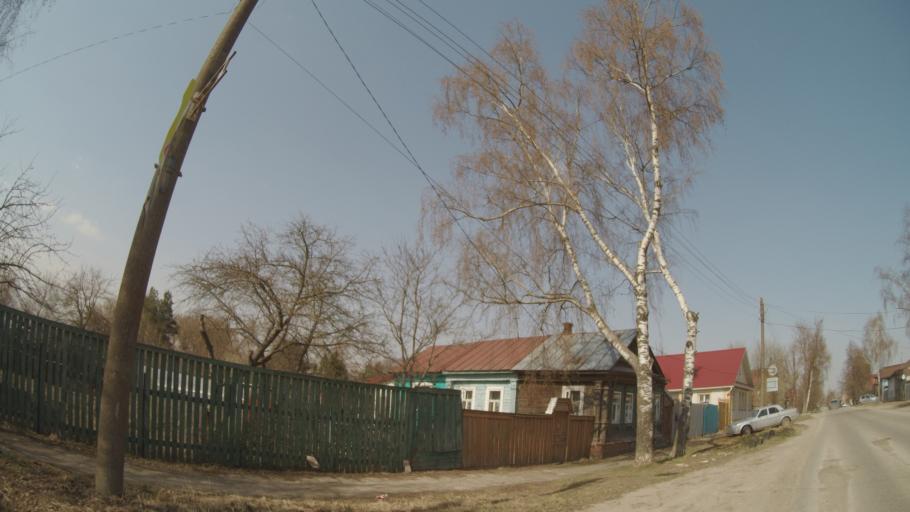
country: RU
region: Nizjnij Novgorod
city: Arzamas
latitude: 55.3871
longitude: 43.8238
